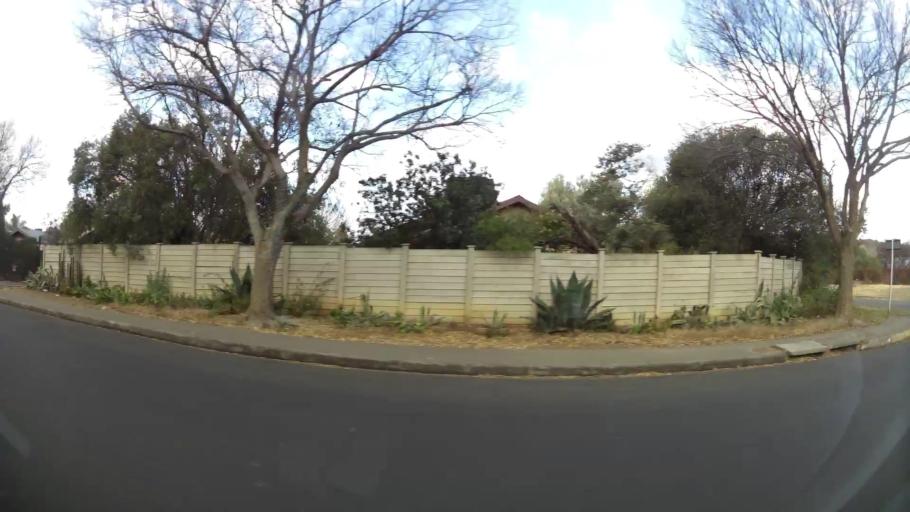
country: ZA
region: Orange Free State
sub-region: Mangaung Metropolitan Municipality
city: Bloemfontein
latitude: -29.0935
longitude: 26.2035
